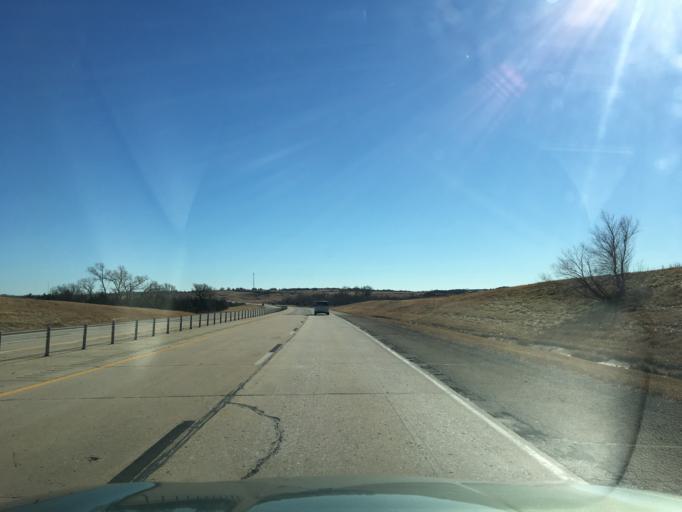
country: US
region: Oklahoma
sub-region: Payne County
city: Stillwater
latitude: 36.2596
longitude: -96.9725
